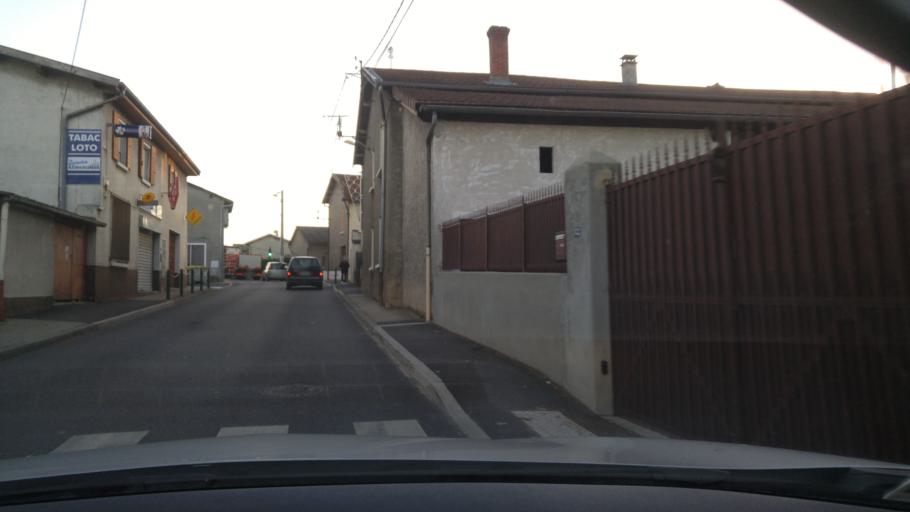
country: FR
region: Rhone-Alpes
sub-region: Departement de l'Isere
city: Tignieu-Jameyzieu
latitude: 45.7364
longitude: 5.1874
